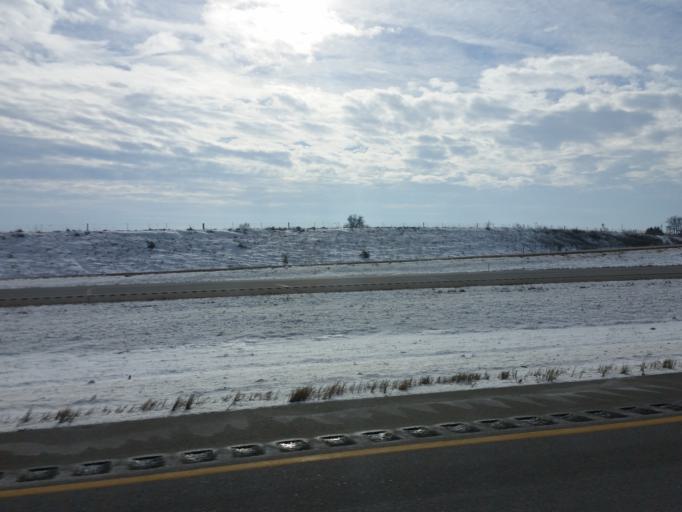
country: US
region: Iowa
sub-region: Buchanan County
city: Independence
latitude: 42.4618
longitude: -91.7497
